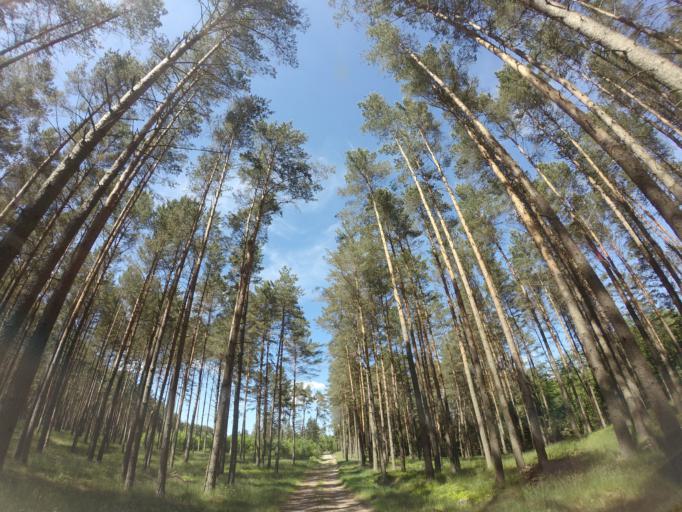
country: PL
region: West Pomeranian Voivodeship
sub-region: Powiat choszczenski
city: Drawno
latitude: 53.1425
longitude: 15.7865
